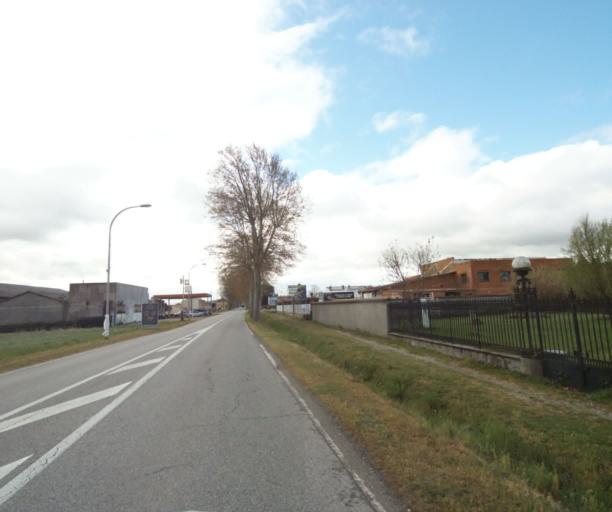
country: FR
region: Midi-Pyrenees
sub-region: Departement de l'Ariege
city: Saverdun
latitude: 43.2458
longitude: 1.5691
